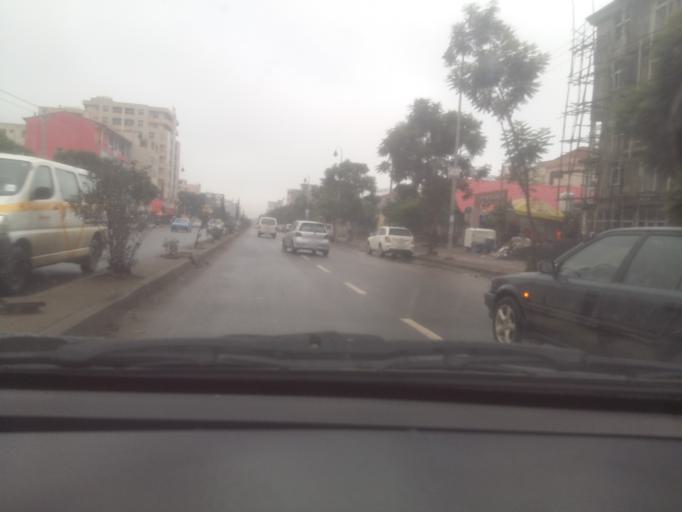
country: ET
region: Adis Abeba
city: Addis Ababa
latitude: 8.9491
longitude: 38.7224
